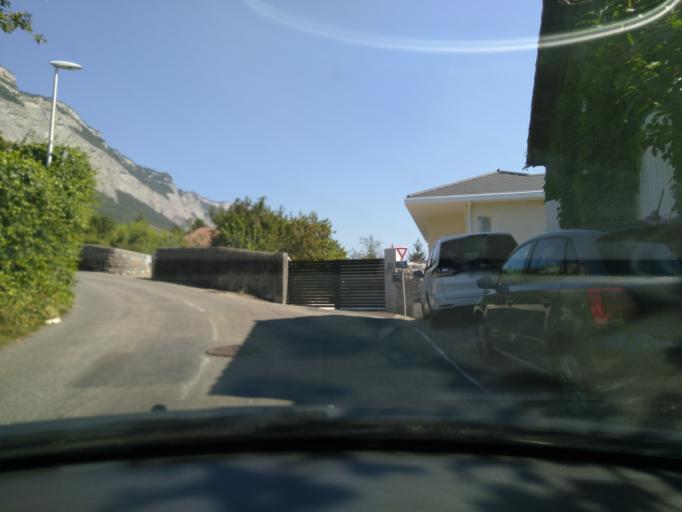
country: FR
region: Rhone-Alpes
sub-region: Departement de l'Isere
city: Meylan
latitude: 45.2227
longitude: 5.7820
